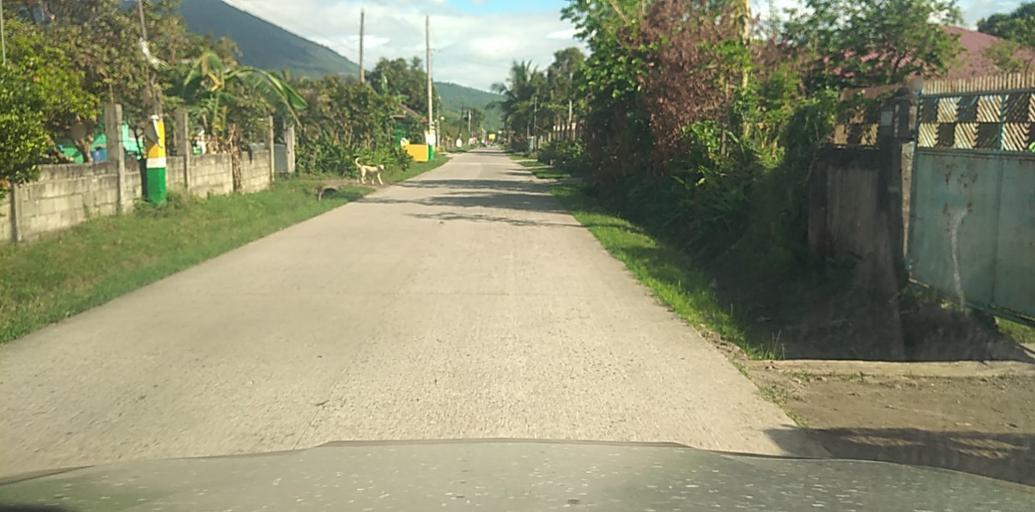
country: PH
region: Central Luzon
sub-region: Province of Pampanga
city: Buensuseso
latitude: 15.1930
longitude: 120.6824
